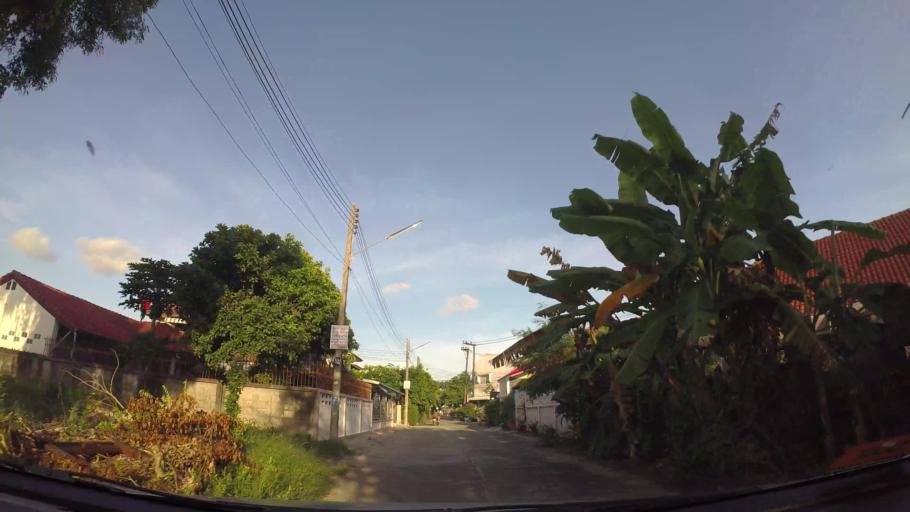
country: TH
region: Rayong
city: Rayong
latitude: 12.6812
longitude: 101.2904
